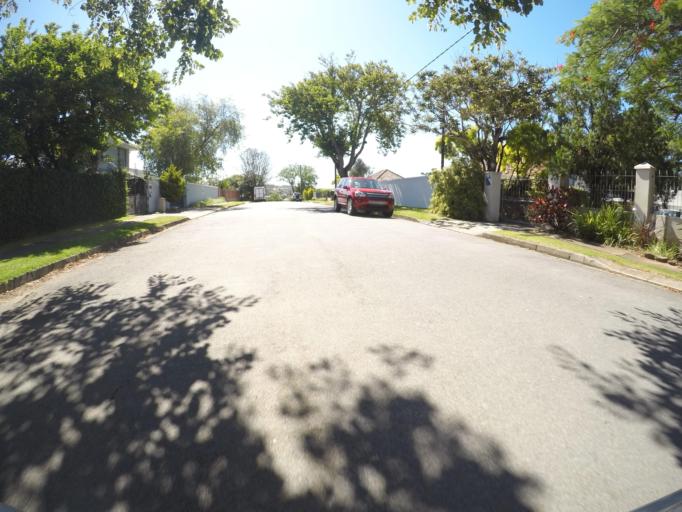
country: ZA
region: Eastern Cape
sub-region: Buffalo City Metropolitan Municipality
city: East London
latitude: -32.9833
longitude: 27.9283
